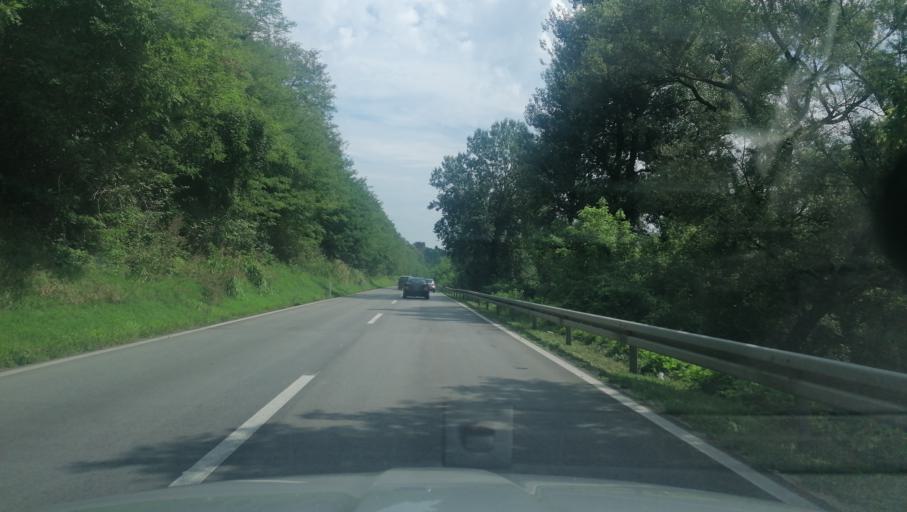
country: BA
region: Federation of Bosnia and Herzegovina
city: Odzak
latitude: 44.9698
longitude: 18.2572
